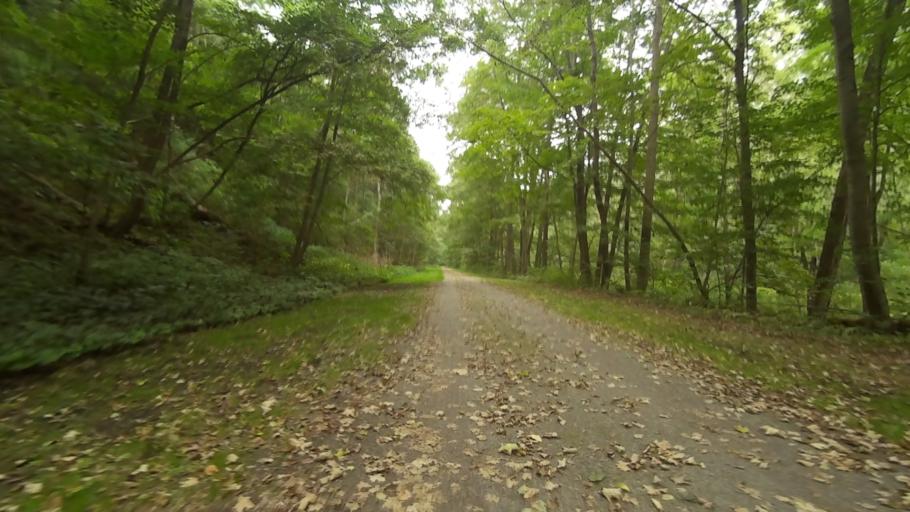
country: US
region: Pennsylvania
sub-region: Blair County
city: Williamsburg
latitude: 40.5579
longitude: -78.1410
